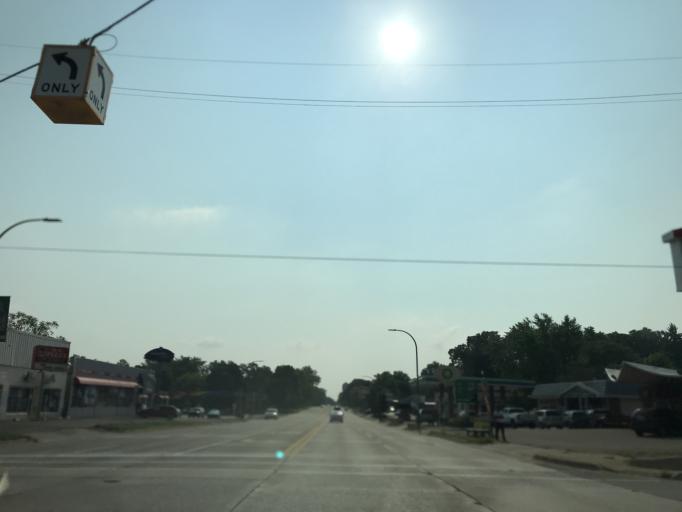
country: US
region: Michigan
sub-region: Washtenaw County
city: Ypsilanti
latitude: 42.2473
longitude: -83.6376
